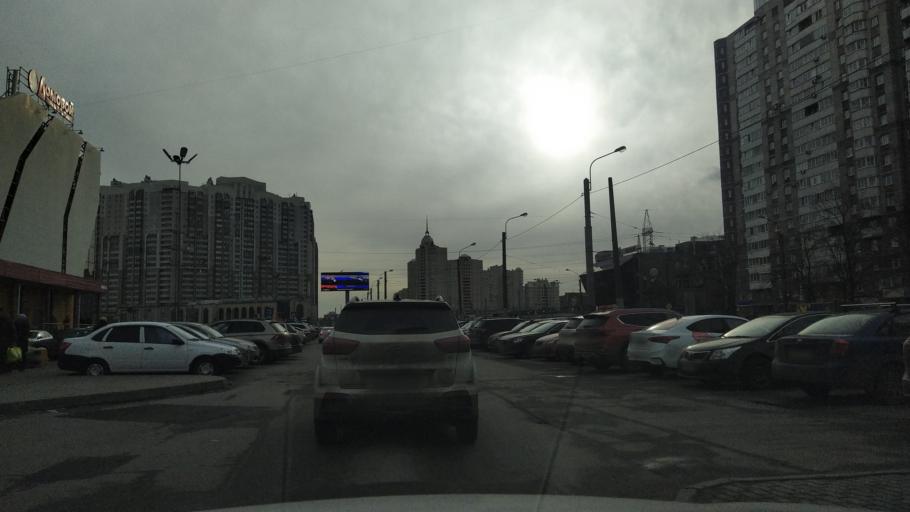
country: RU
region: Leningrad
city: Chernaya Rechka
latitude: 60.0056
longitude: 30.2976
